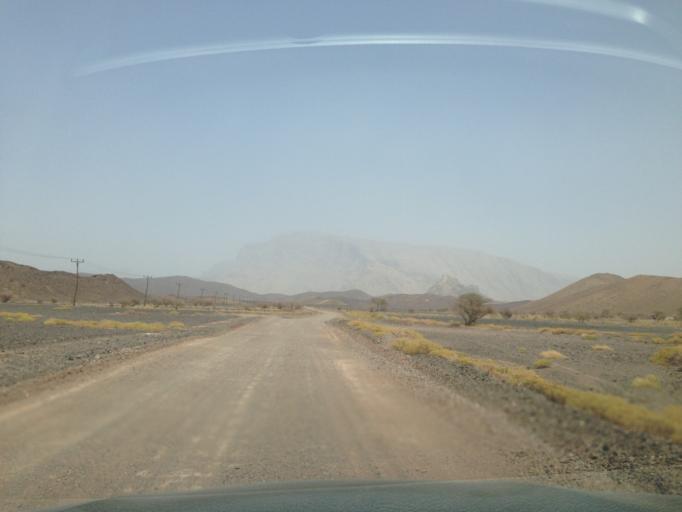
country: OM
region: Az Zahirah
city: `Ibri
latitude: 23.2071
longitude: 56.8486
